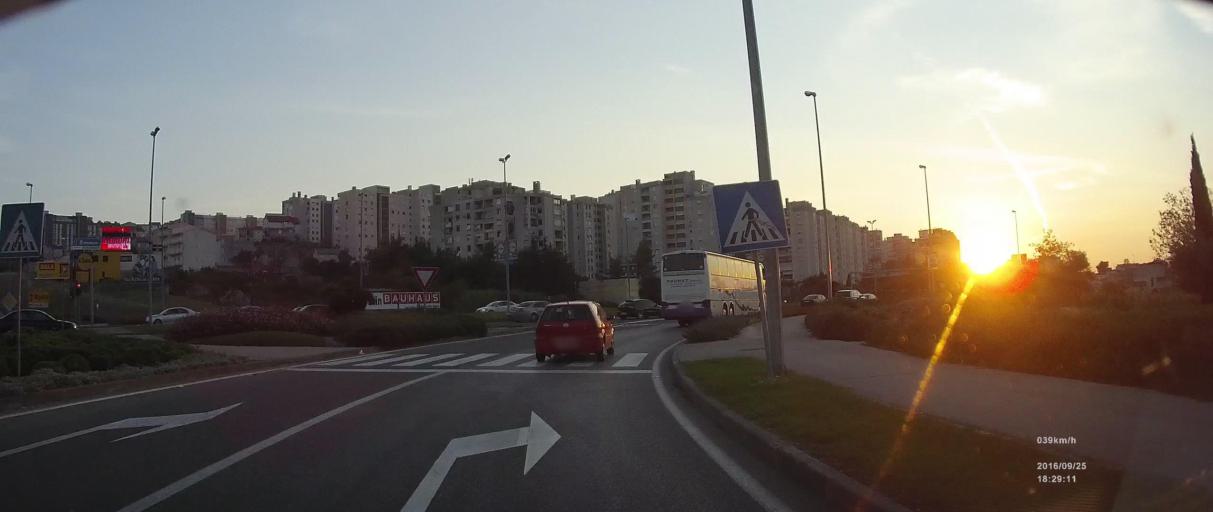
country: HR
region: Splitsko-Dalmatinska
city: Vranjic
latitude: 43.5189
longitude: 16.4808
